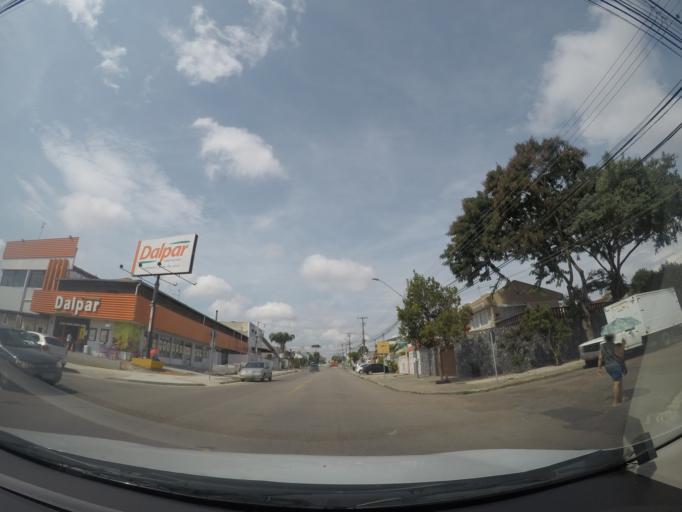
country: BR
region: Parana
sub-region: Curitiba
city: Curitiba
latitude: -25.4894
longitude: -49.2806
